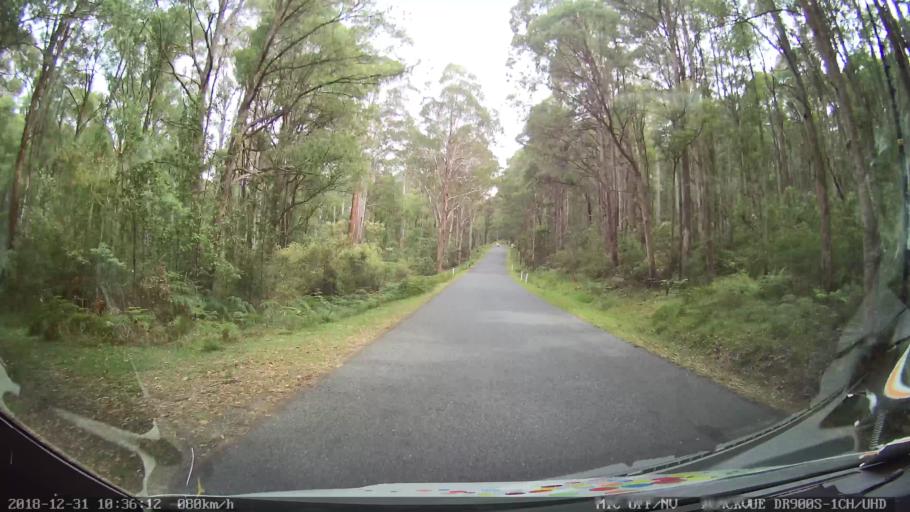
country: AU
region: New South Wales
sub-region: Snowy River
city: Jindabyne
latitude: -36.4288
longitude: 148.1705
